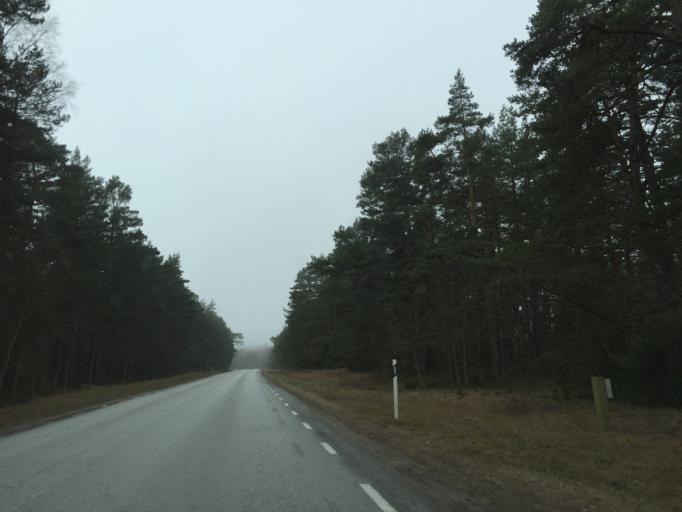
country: EE
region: Saare
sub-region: Kuressaare linn
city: Kuressaare
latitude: 58.1943
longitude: 22.2748
